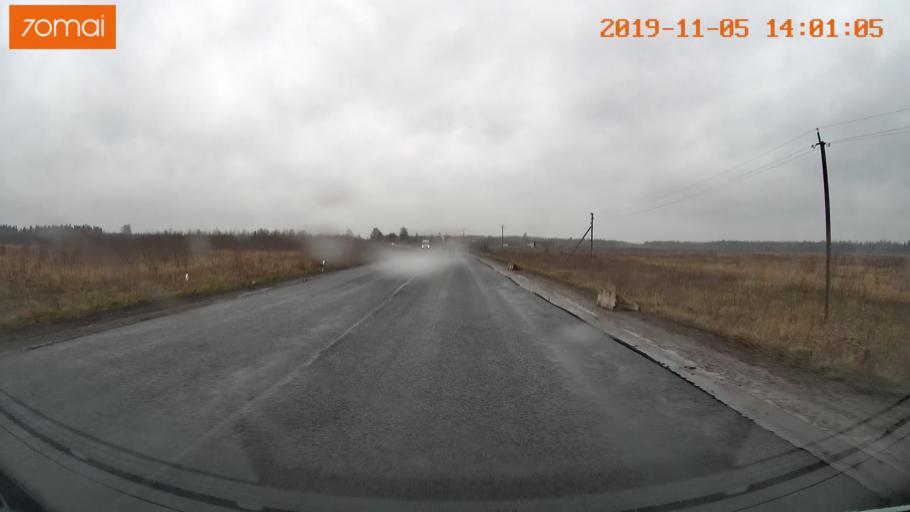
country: RU
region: Ivanovo
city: Kitovo
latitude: 57.0114
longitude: 41.2356
